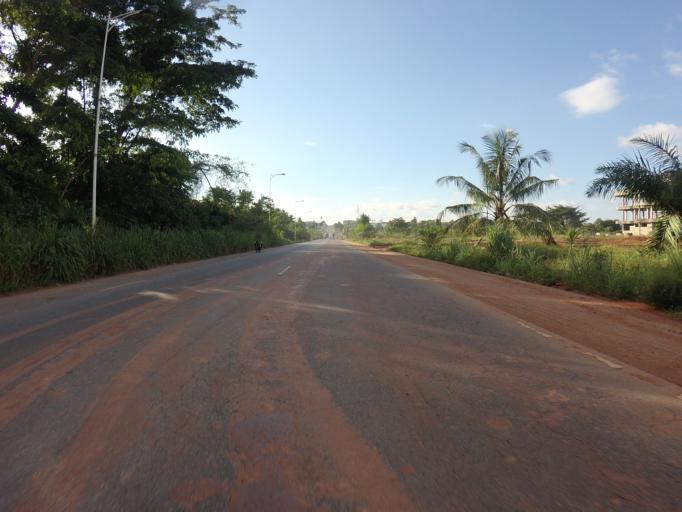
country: GH
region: Ashanti
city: Tafo
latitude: 6.9293
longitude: -1.6643
